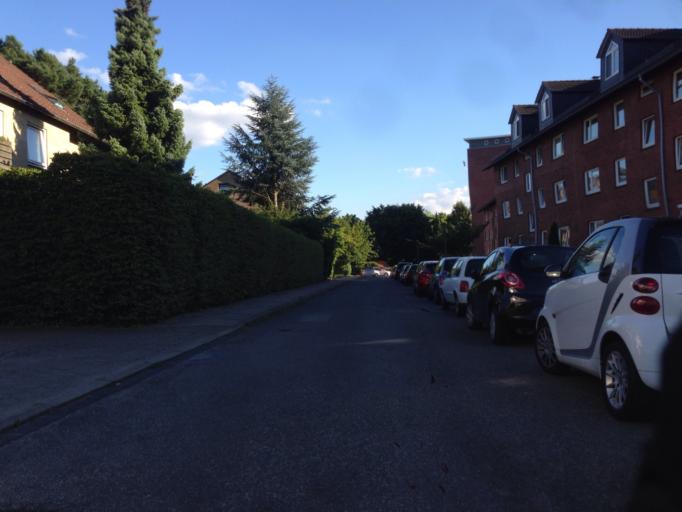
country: DE
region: Hamburg
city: Farmsen-Berne
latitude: 53.5862
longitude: 10.1169
